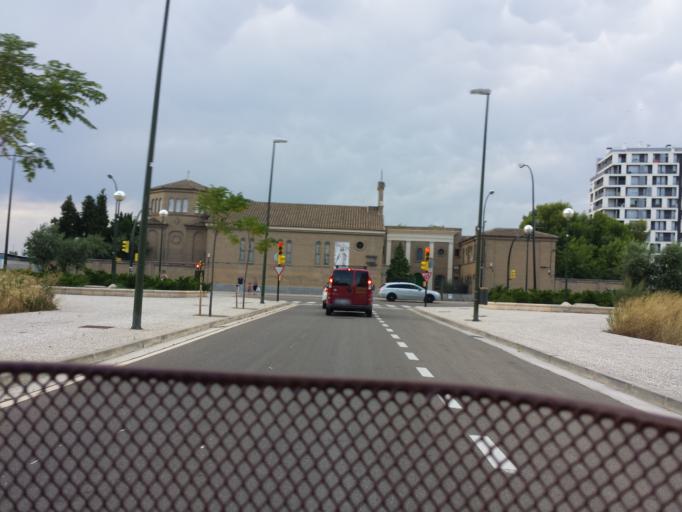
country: ES
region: Aragon
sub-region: Provincia de Zaragoza
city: Zaragoza
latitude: 41.6655
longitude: -0.8556
